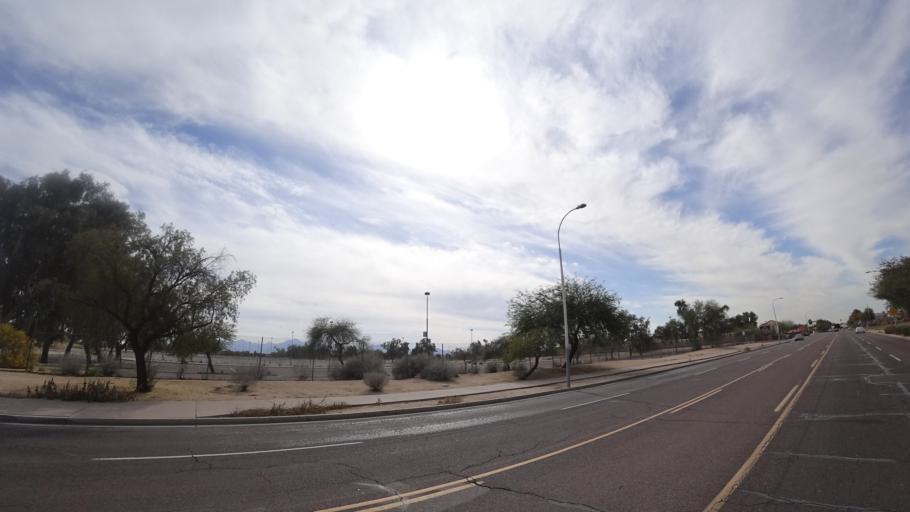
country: US
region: Arizona
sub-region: Maricopa County
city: Tolleson
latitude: 33.4727
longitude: -112.2346
